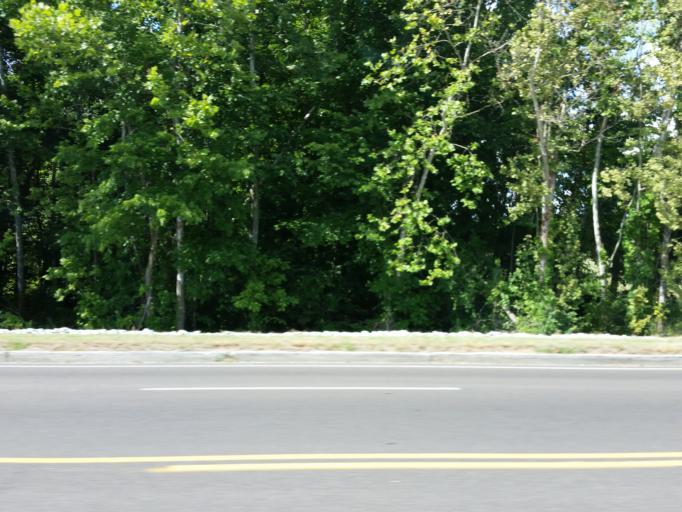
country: US
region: Tennessee
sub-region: Henderson County
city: Lexington
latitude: 35.6582
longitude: -88.4149
